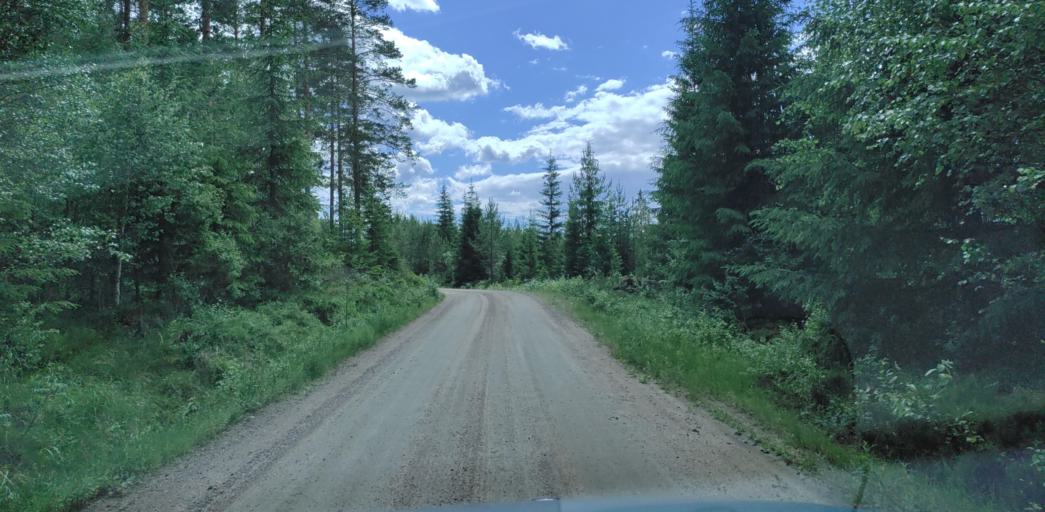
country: SE
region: Vaermland
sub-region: Hagfors Kommun
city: Ekshaerad
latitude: 60.0686
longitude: 13.2907
